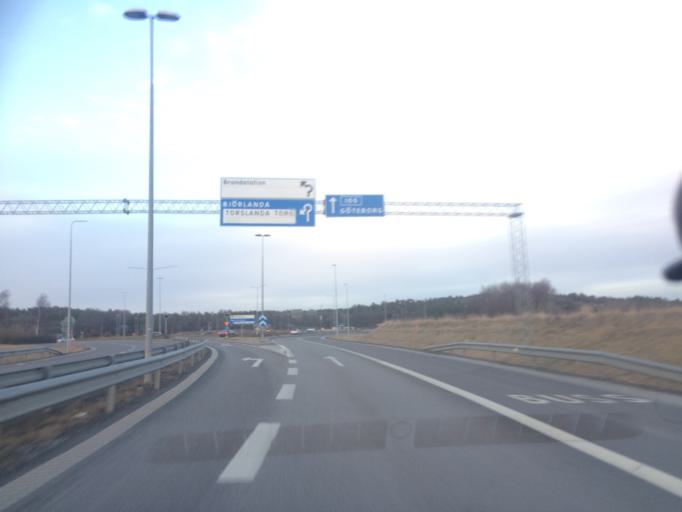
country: SE
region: Vaestra Goetaland
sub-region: Goteborg
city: Torslanda
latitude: 57.7150
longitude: 11.7924
